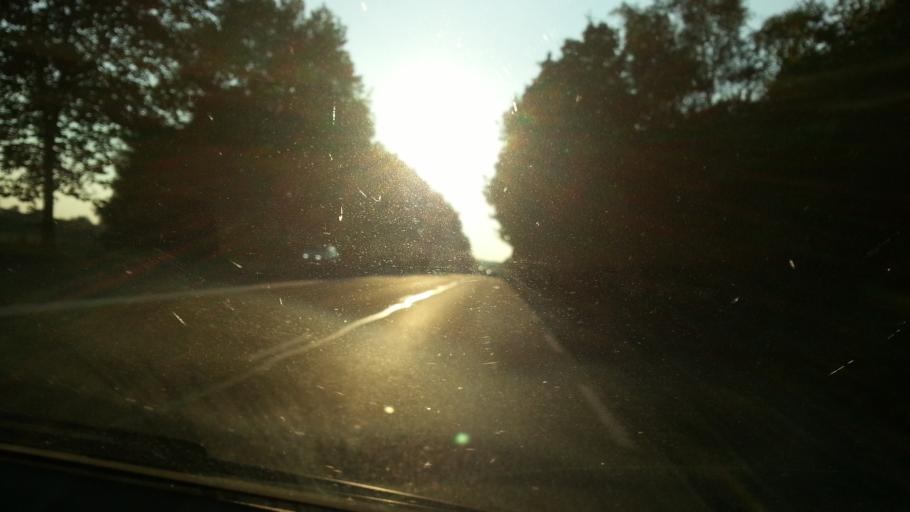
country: FR
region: Picardie
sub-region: Departement de l'Oise
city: Brenouille
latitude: 49.3078
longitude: 2.5387
